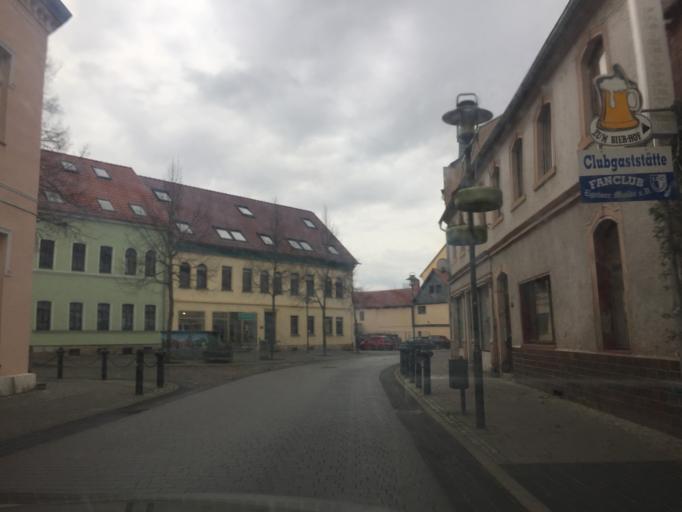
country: DE
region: Saxony-Anhalt
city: Egeln
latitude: 51.9435
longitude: 11.4316
